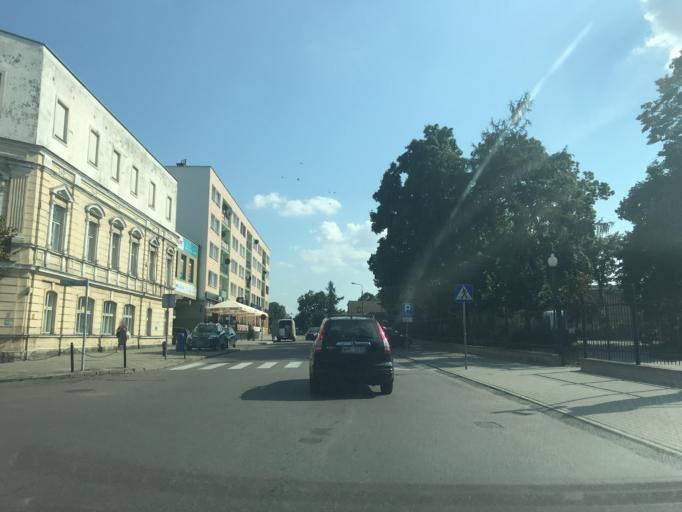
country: PL
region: Masovian Voivodeship
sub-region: Powiat mlawski
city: Mlawa
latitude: 53.1125
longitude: 20.3794
